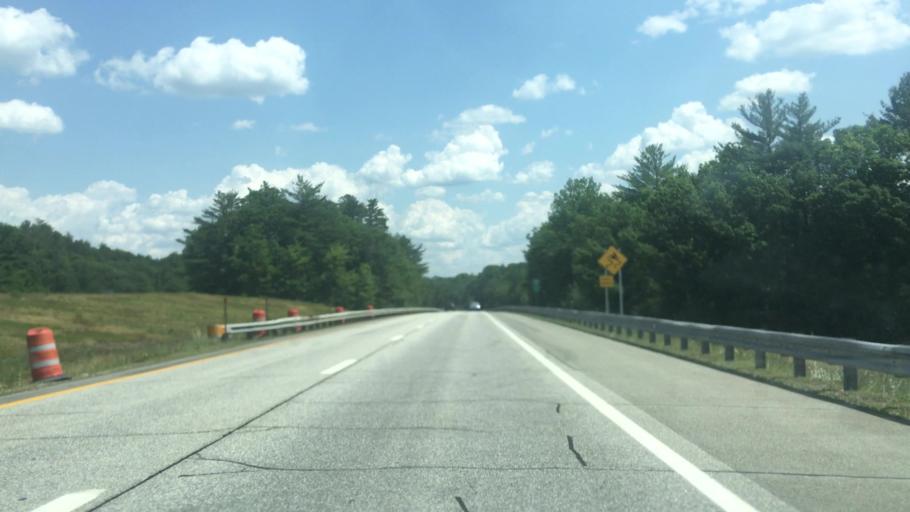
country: US
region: New Hampshire
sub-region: Merrimack County
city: Contoocook
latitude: 43.2709
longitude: -71.7849
